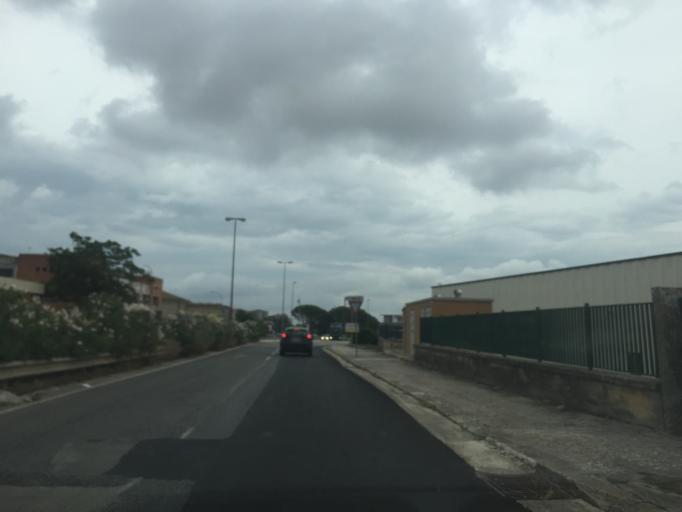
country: IT
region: Sicily
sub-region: Ragusa
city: Ragusa
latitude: 36.8999
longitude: 14.7050
